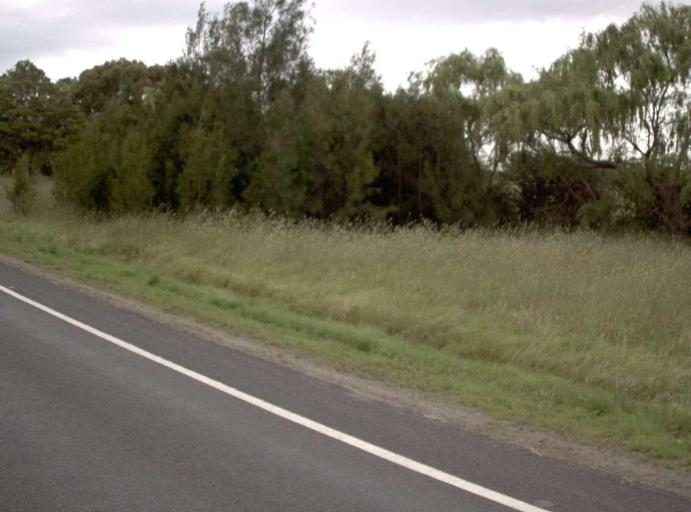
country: AU
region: Victoria
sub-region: Wellington
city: Sale
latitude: -38.0709
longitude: 147.0734
